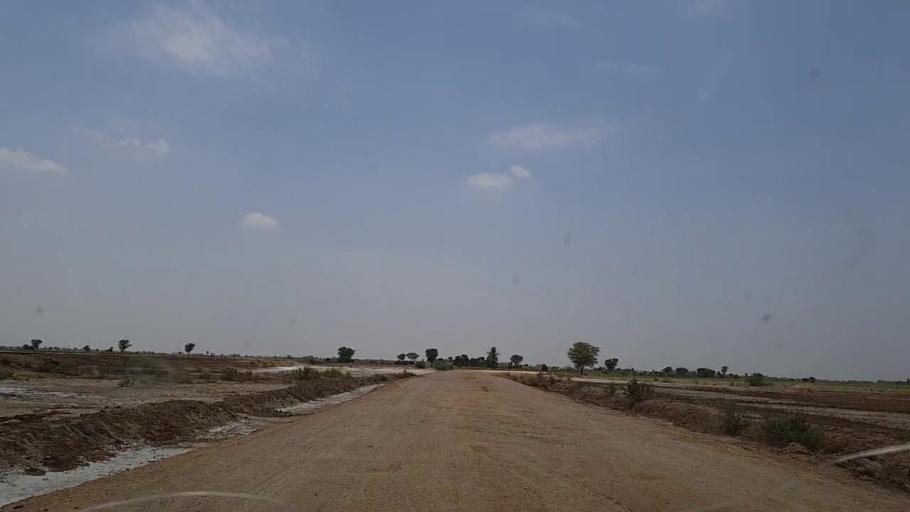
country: PK
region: Sindh
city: Phulji
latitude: 26.8024
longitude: 67.6346
